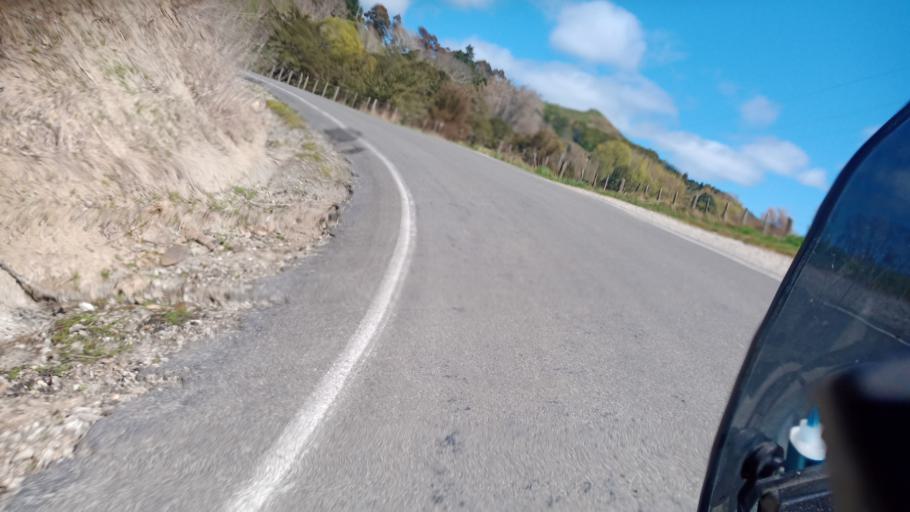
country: NZ
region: Gisborne
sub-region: Gisborne District
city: Gisborne
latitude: -38.7855
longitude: 177.7869
